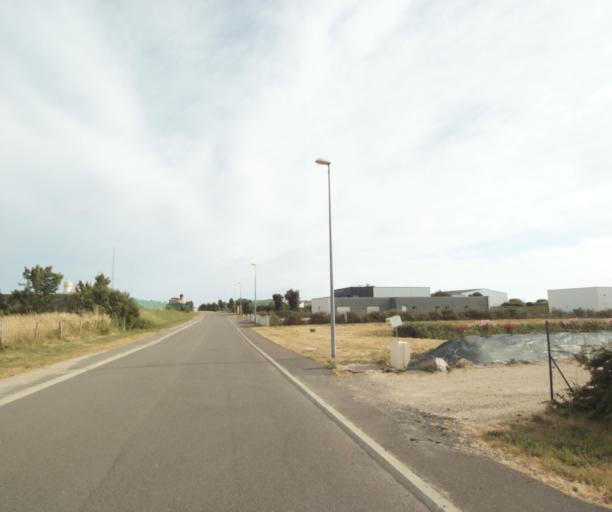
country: FR
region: Pays de la Loire
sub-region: Departement de la Vendee
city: Chateau-d'Olonne
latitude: 46.4943
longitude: -1.7299
